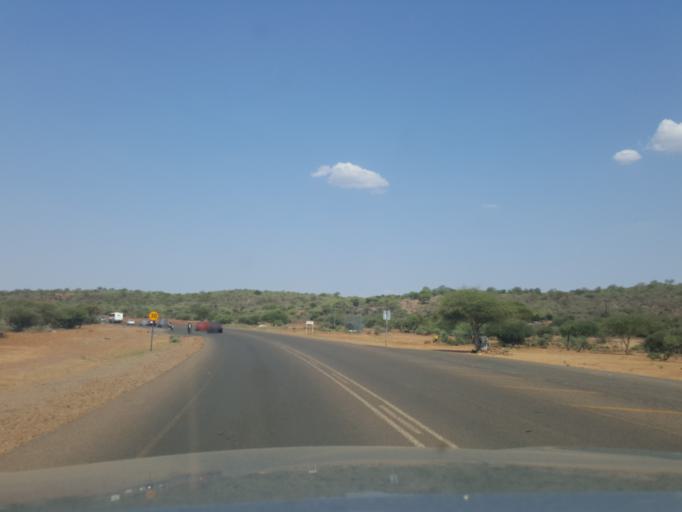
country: BW
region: South East
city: Ramotswa
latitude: -24.8618
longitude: 25.8354
